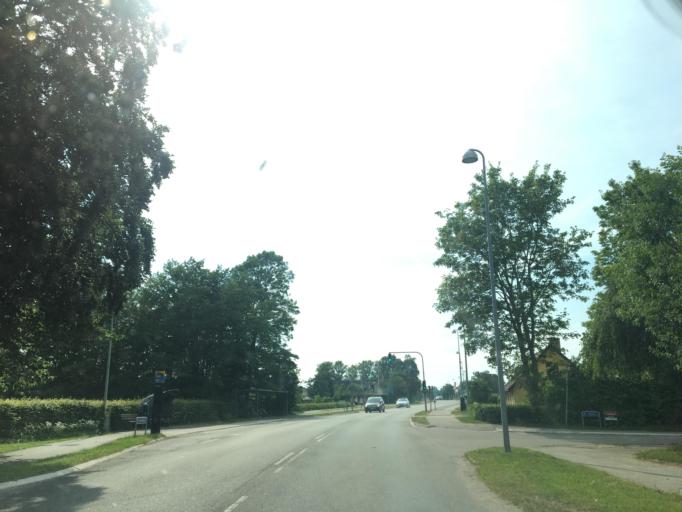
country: DK
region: Zealand
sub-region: Greve Kommune
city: Tune
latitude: 55.5960
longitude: 12.1934
